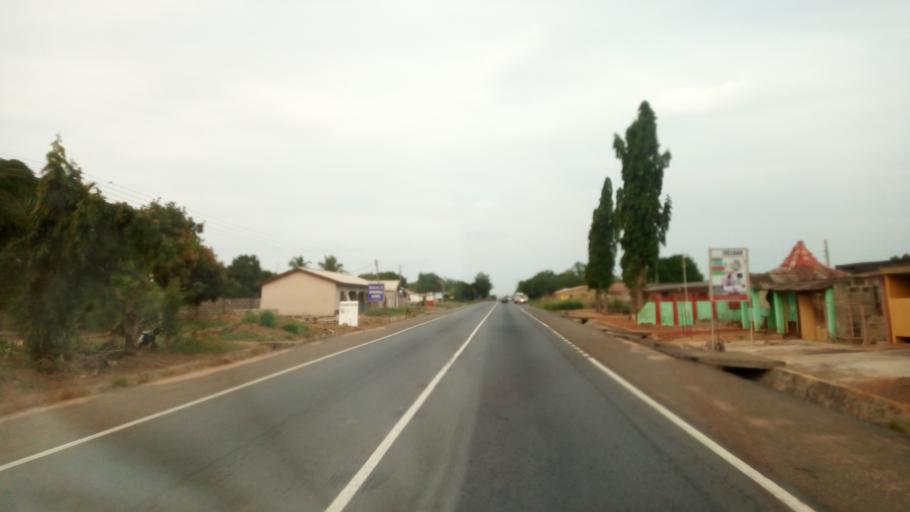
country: GH
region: Volta
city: Keta
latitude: 6.0545
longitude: 0.9811
